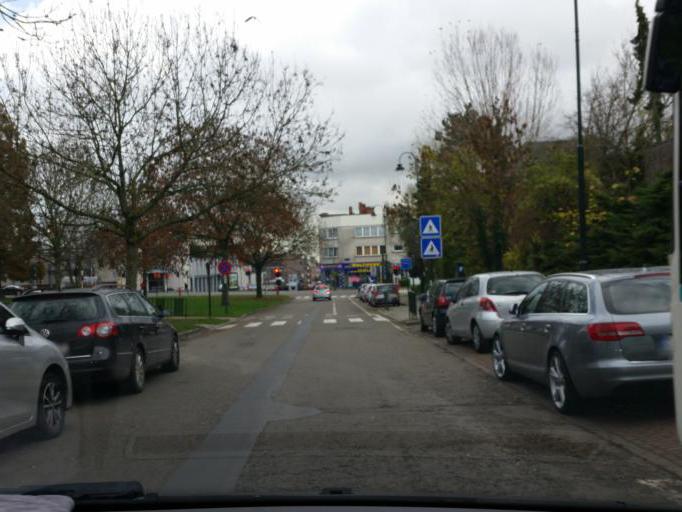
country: BE
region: Flanders
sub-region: Provincie Vlaams-Brabant
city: Grimbergen
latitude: 50.8976
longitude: 4.3554
